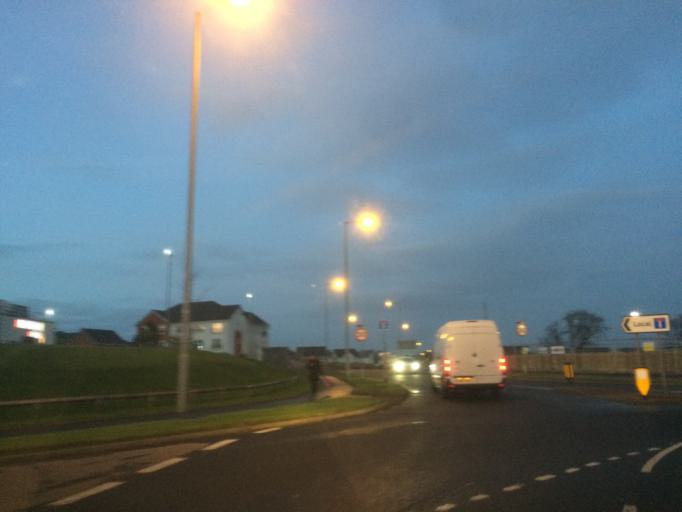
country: GB
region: Scotland
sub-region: East Renfrewshire
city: Newton Mearns
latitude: 55.7838
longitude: -4.3474
